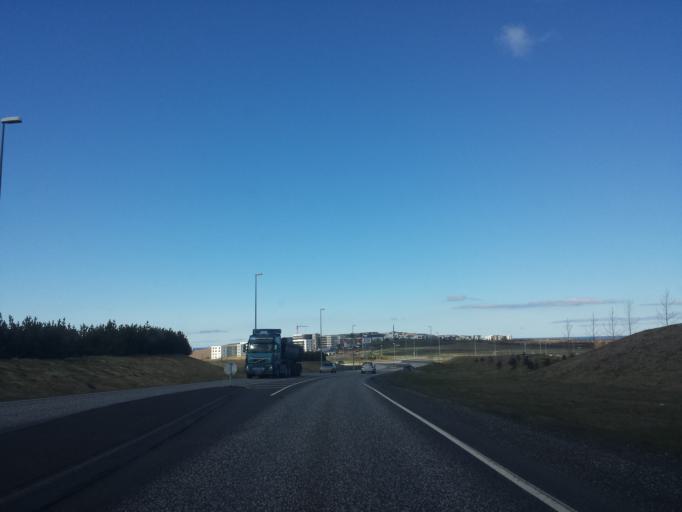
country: IS
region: Capital Region
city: Reykjavik
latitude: 64.0894
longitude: -21.8522
